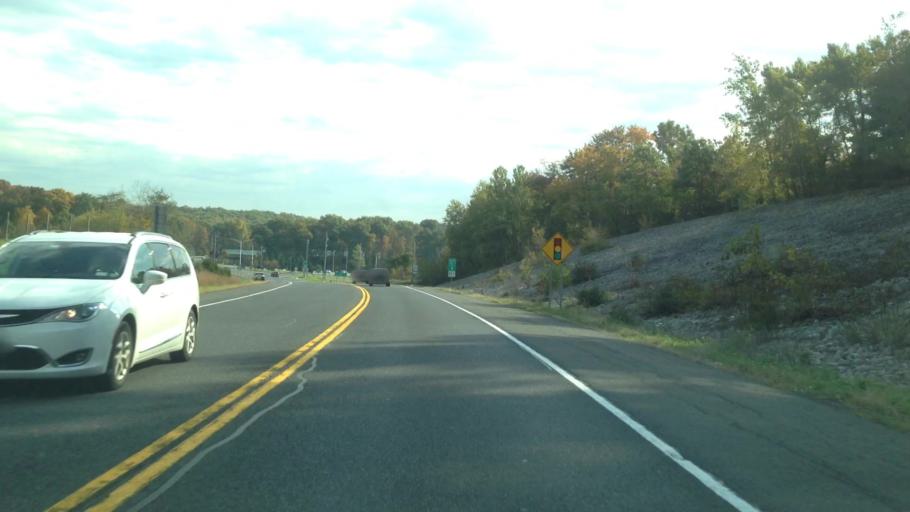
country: US
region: New York
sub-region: Ulster County
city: Highland
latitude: 41.7417
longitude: -73.9683
